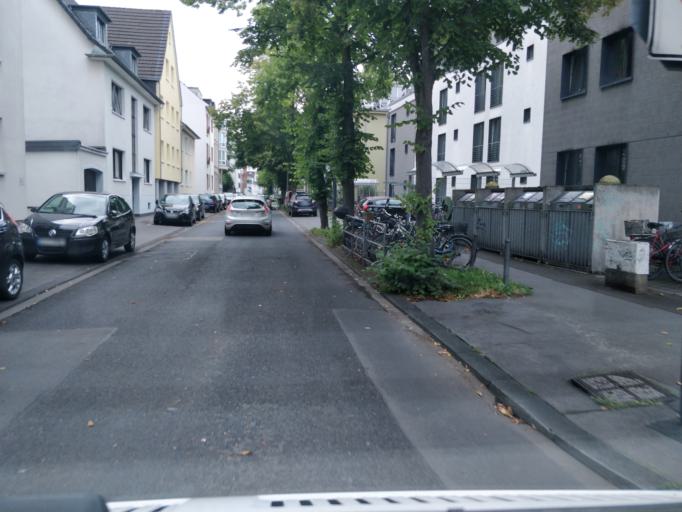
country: DE
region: North Rhine-Westphalia
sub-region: Regierungsbezirk Koln
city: Neustadt/Sued
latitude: 50.9276
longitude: 6.9144
